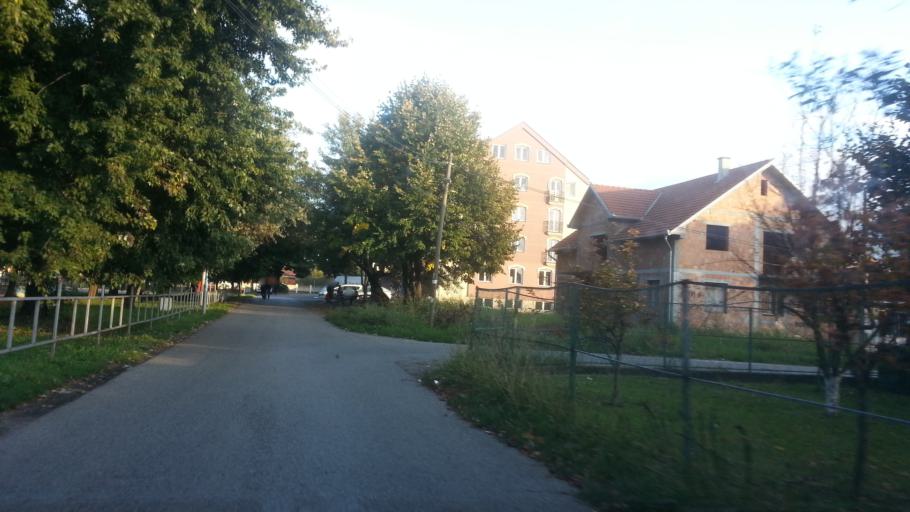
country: RS
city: Novi Banovci
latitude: 44.8946
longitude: 20.2900
